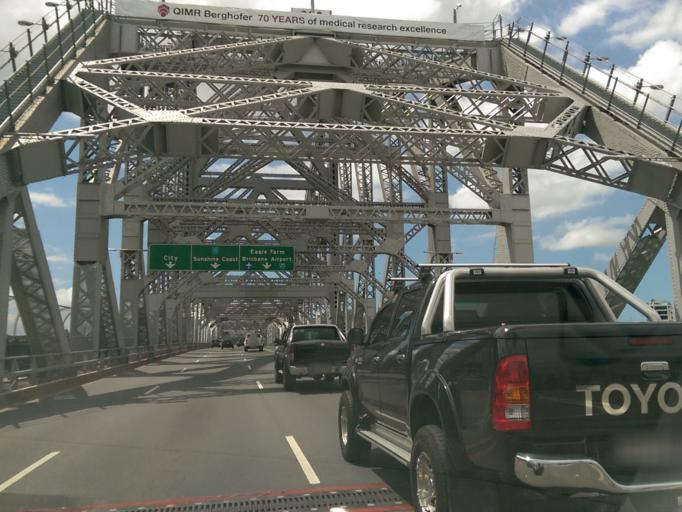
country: AU
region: Queensland
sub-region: Brisbane
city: Brisbane
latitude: -27.4658
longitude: 153.0358
